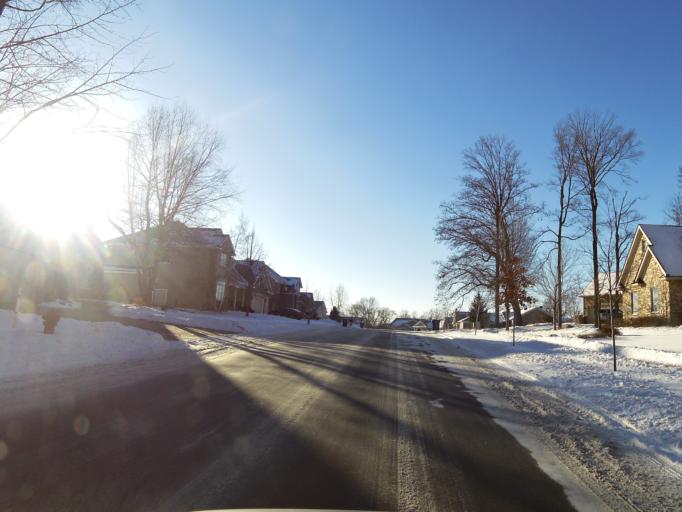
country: US
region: Minnesota
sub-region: Scott County
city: Prior Lake
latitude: 44.7292
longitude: -93.4439
